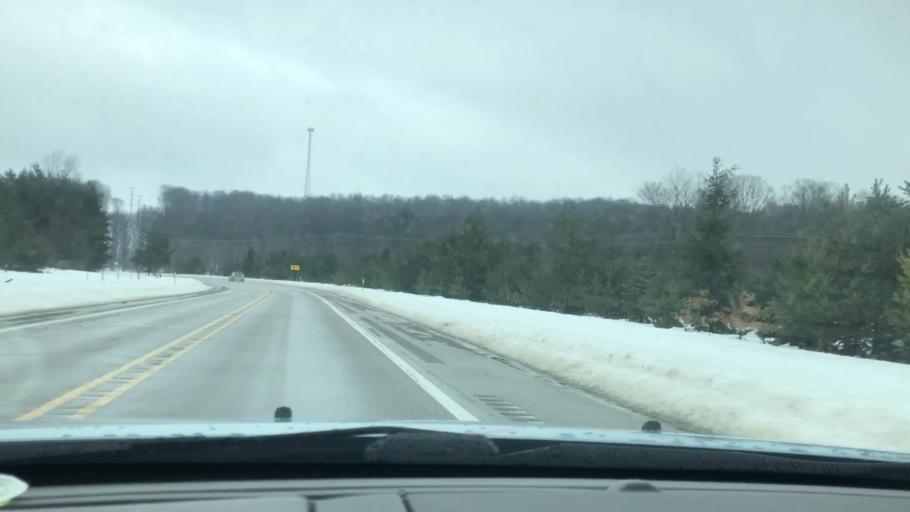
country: US
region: Michigan
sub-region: Charlevoix County
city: Boyne City
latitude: 45.0826
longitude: -84.9225
